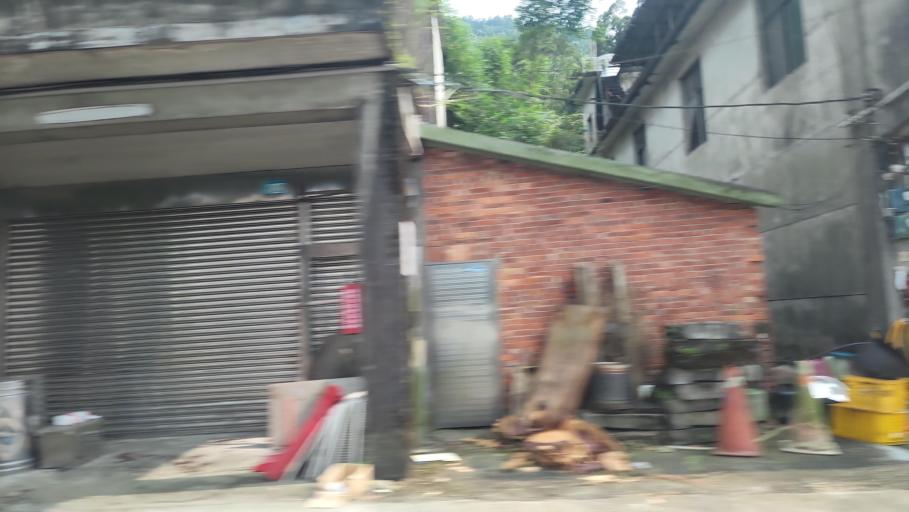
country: TW
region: Taiwan
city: Daxi
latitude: 24.9053
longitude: 121.3991
